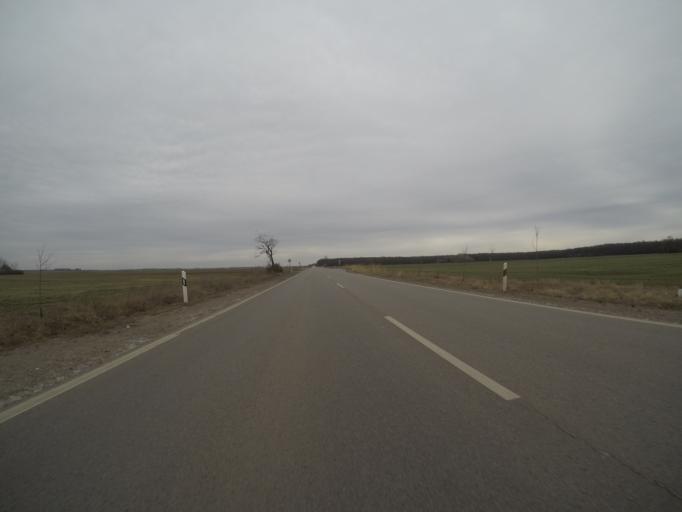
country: HU
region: Jasz-Nagykun-Szolnok
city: Jaszapati
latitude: 47.5116
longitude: 20.0745
